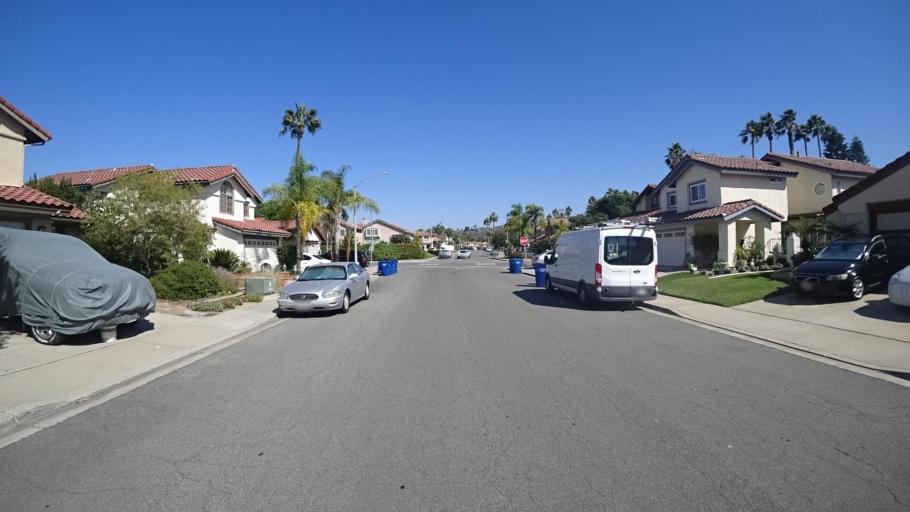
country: US
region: California
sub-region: San Diego County
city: Rancho San Diego
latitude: 32.7494
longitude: -116.9350
